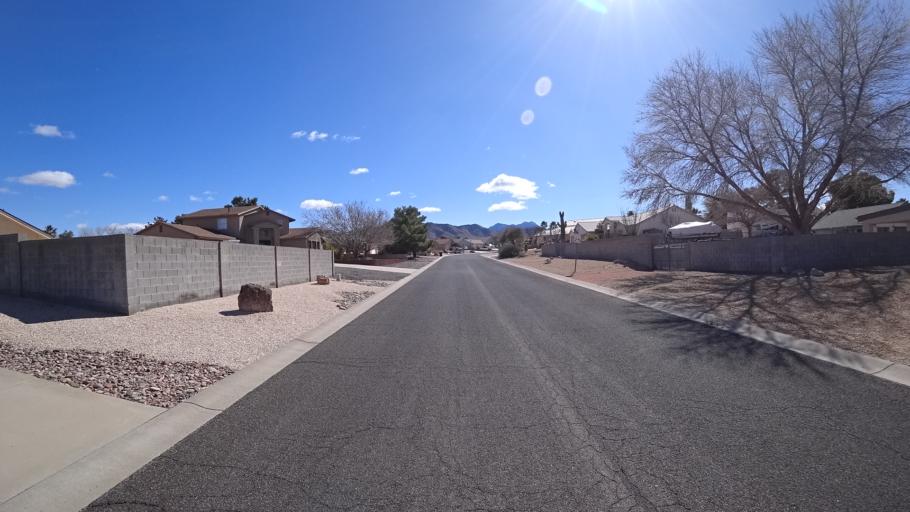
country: US
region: Arizona
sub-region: Mohave County
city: Kingman
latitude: 35.2003
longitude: -113.9668
